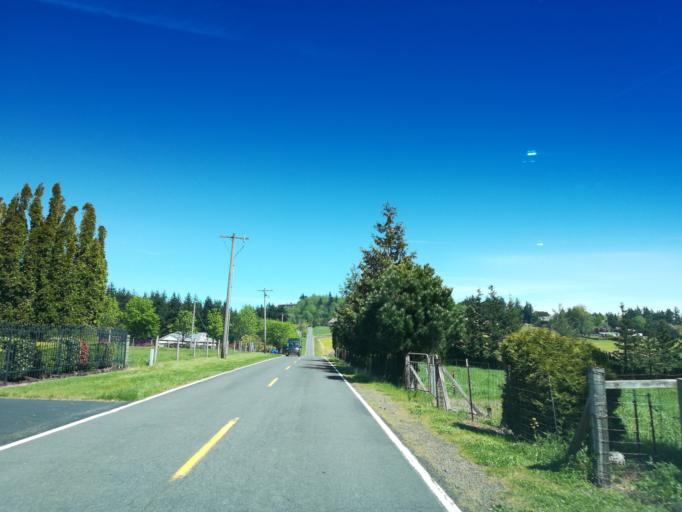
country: US
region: Oregon
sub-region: Multnomah County
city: Troutdale
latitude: 45.5334
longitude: -122.3594
